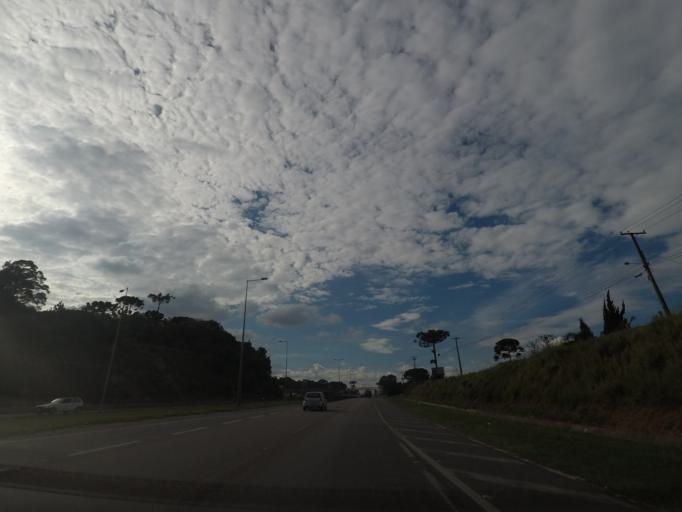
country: BR
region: Parana
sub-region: Araucaria
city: Araucaria
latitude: -25.6086
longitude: -49.3192
